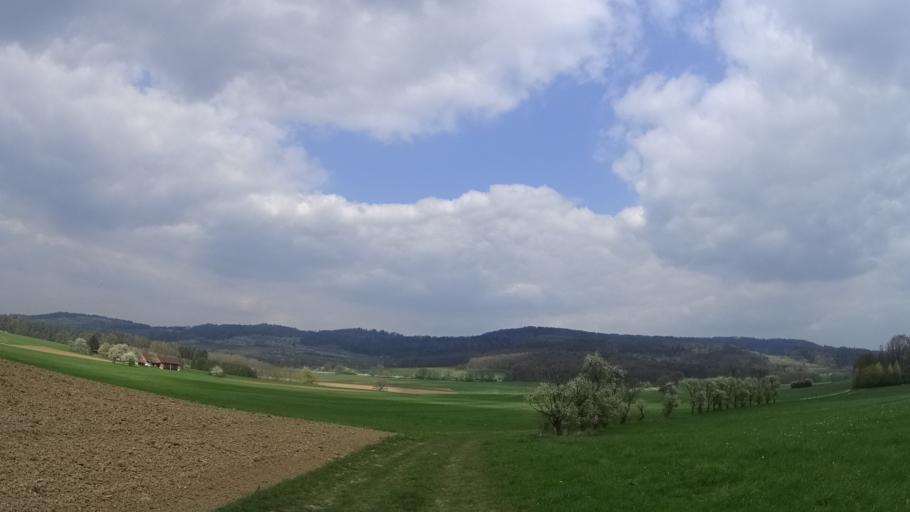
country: DE
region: Bavaria
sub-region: Upper Franconia
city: Kleinsendelbach
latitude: 49.6073
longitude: 11.1773
